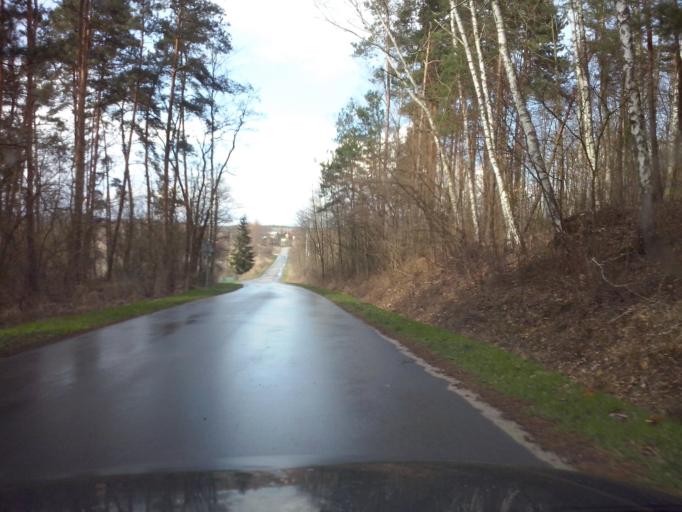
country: PL
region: Subcarpathian Voivodeship
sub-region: Powiat nizanski
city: Bieliny
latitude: 50.4341
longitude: 22.3055
